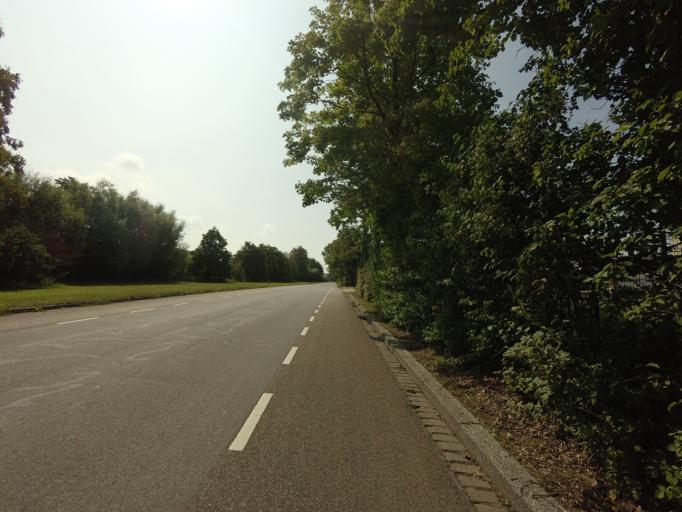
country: NL
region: South Holland
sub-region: Gemeente Sliedrecht
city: Sliedrecht
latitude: 51.8144
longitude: 4.7495
